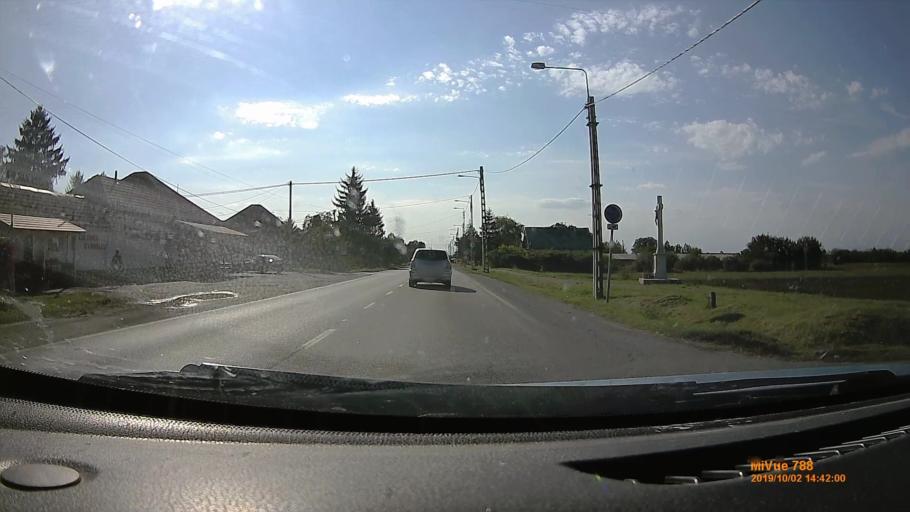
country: HU
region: Heves
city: Szihalom
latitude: 47.7800
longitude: 20.4825
